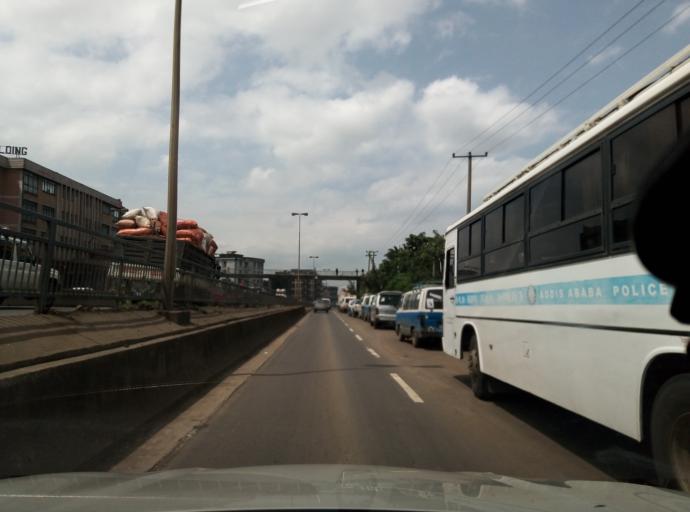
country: ET
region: Adis Abeba
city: Addis Ababa
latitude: 9.0010
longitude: 38.7189
